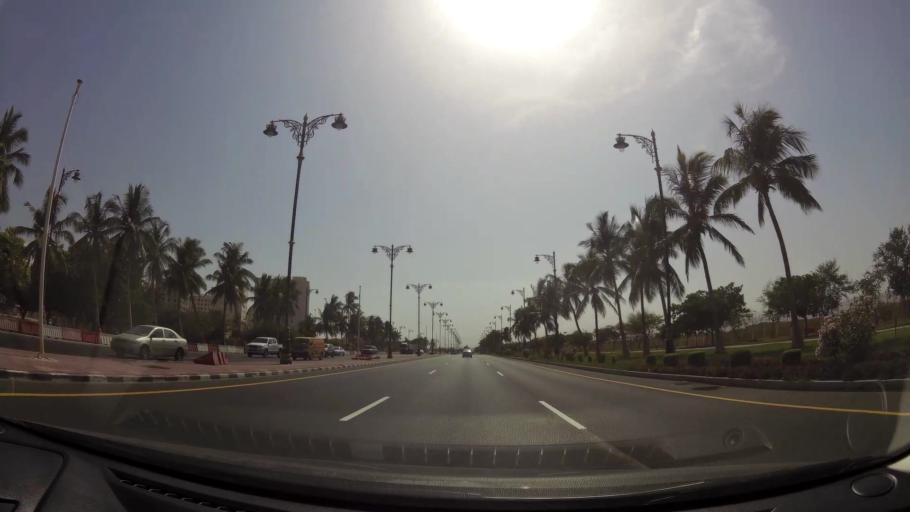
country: OM
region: Zufar
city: Salalah
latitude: 17.0241
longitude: 54.0958
